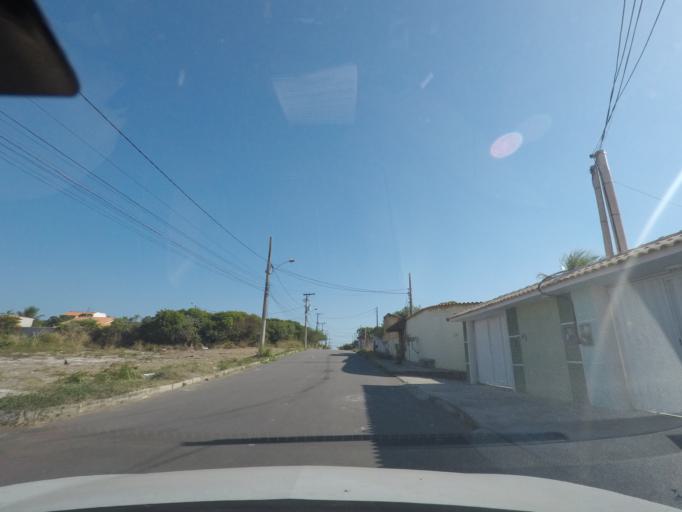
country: BR
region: Rio de Janeiro
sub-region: Marica
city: Marica
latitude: -22.9679
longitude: -42.9190
